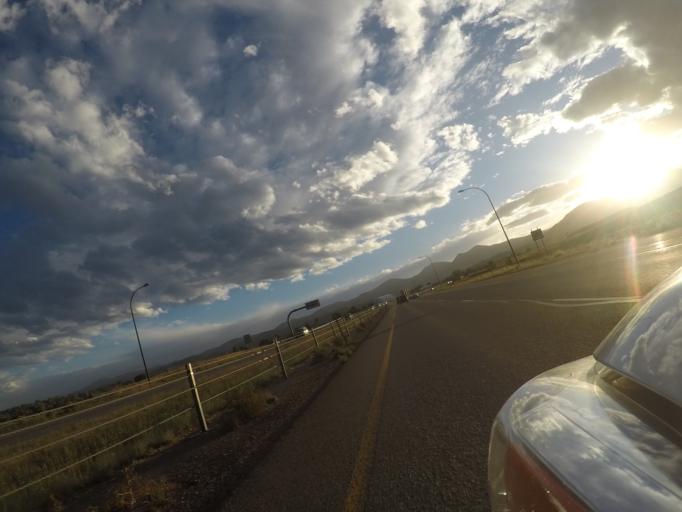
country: US
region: Colorado
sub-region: Jefferson County
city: Ken Caryl
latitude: 39.6416
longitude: -105.1349
